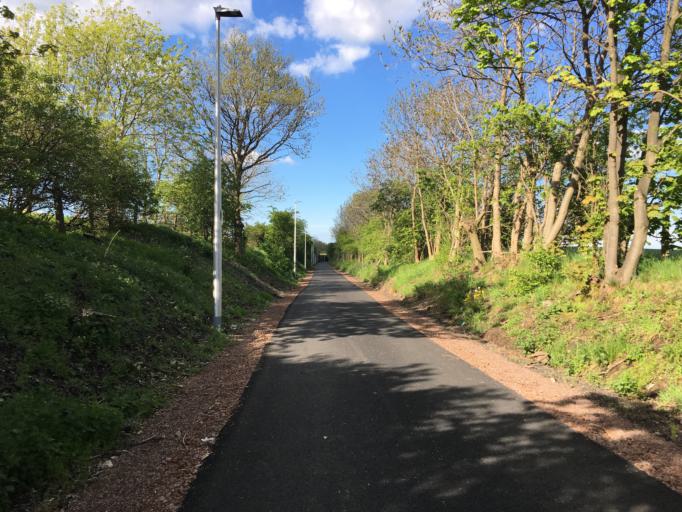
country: GB
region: Scotland
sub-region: Midlothian
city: Loanhead
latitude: 55.8967
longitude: -3.1308
